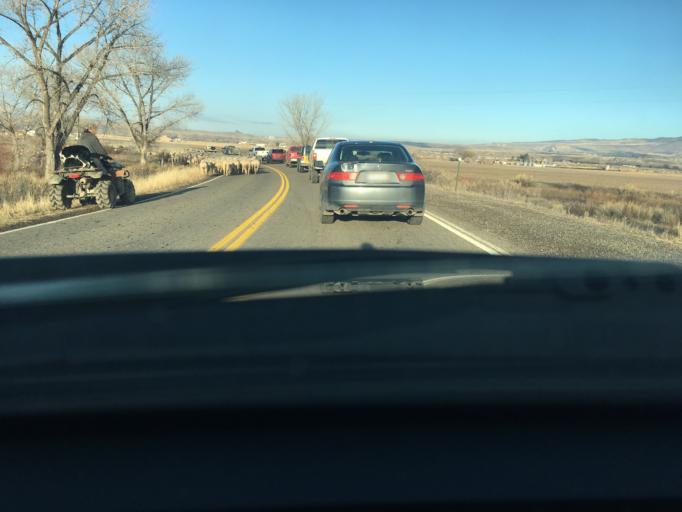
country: US
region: Colorado
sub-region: Delta County
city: Delta
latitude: 38.7486
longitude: -108.1210
